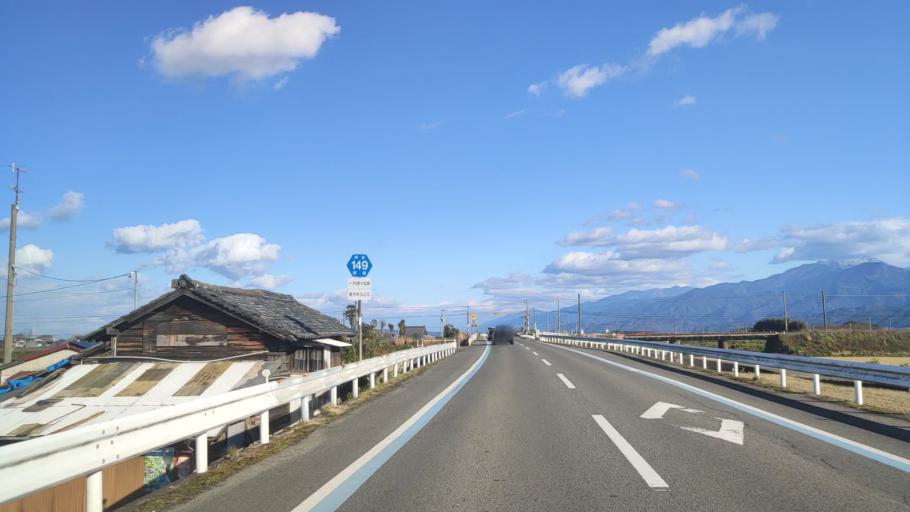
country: JP
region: Ehime
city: Saijo
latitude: 33.9084
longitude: 133.0975
